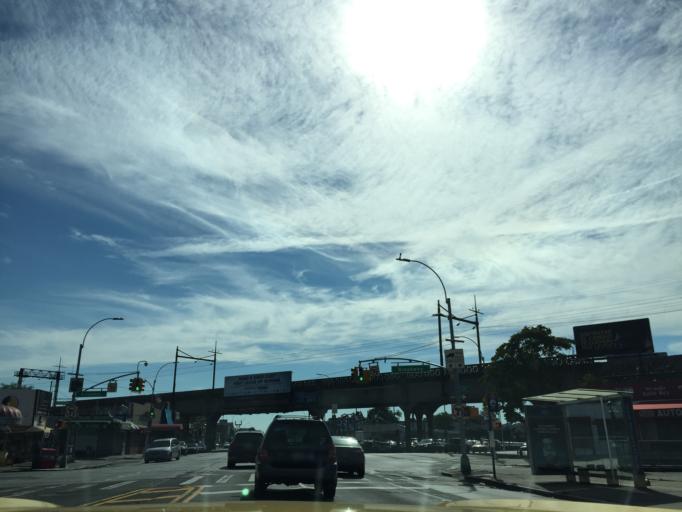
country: US
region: New York
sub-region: Queens County
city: Long Island City
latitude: 40.7533
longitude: -73.9074
